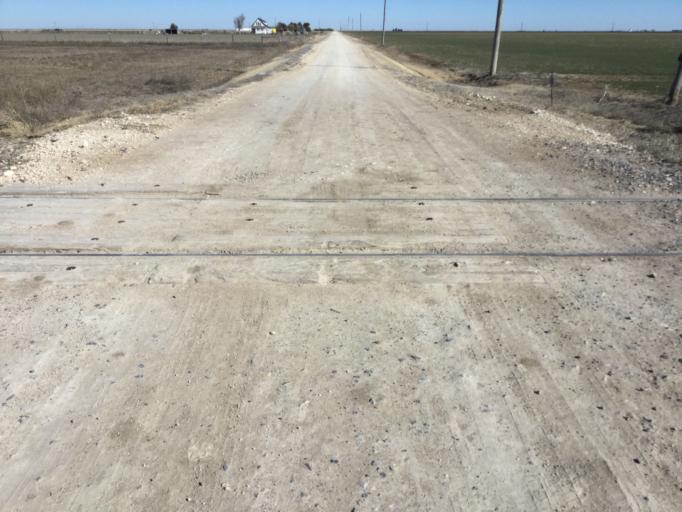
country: US
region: Kansas
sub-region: Scott County
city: Scott City
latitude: 38.4868
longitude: -101.0541
